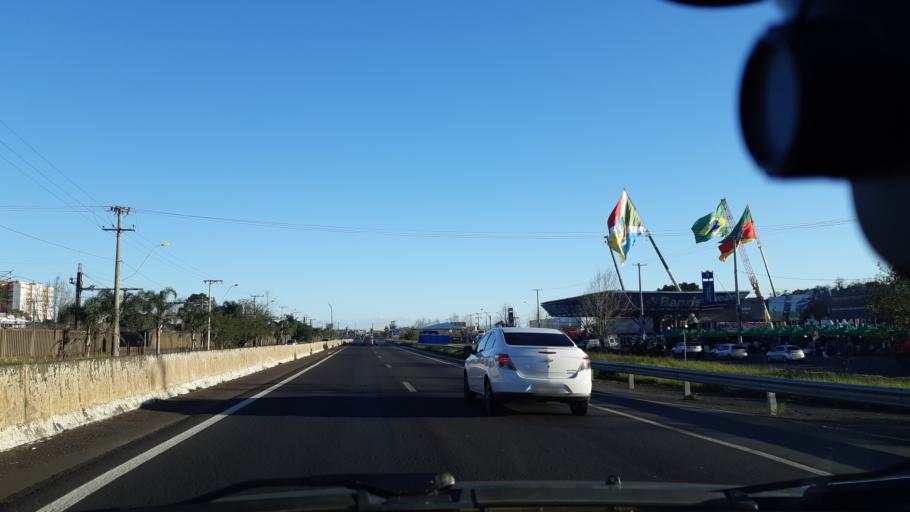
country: BR
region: Rio Grande do Sul
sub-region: Esteio
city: Esteio
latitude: -29.8531
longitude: -51.1799
